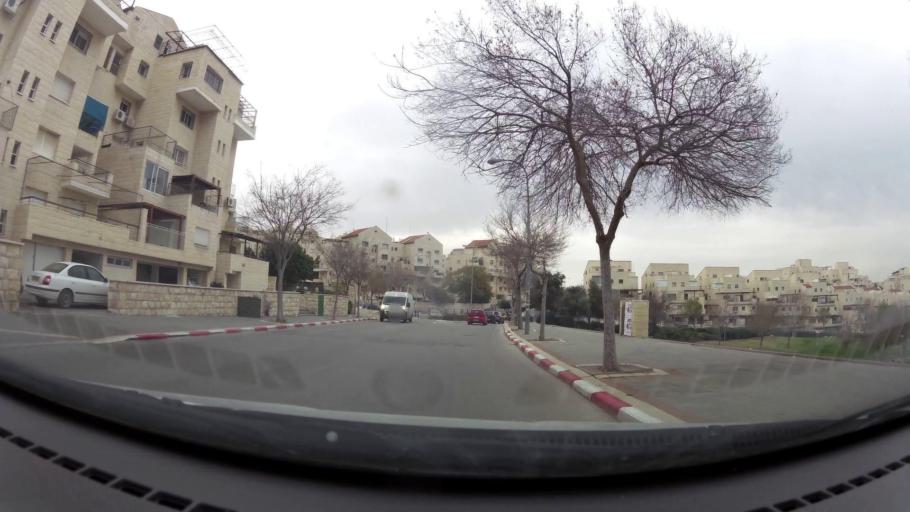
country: IL
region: Jerusalem
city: Bet Shemesh
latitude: 31.7112
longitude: 34.9970
